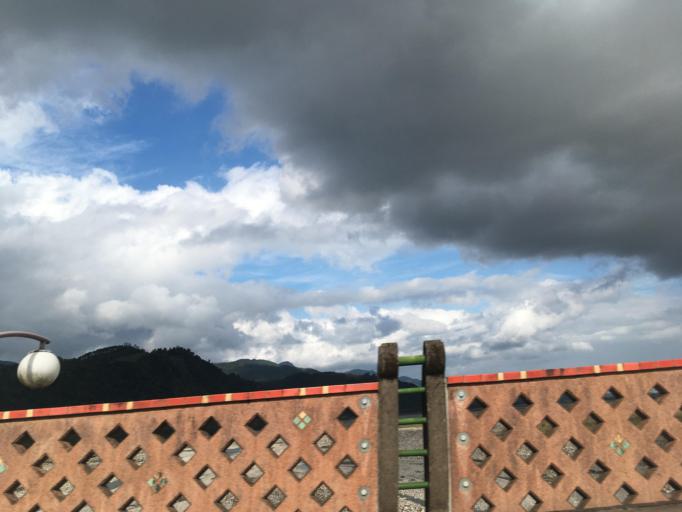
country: TW
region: Taiwan
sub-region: Yilan
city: Yilan
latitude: 24.6690
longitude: 121.6105
